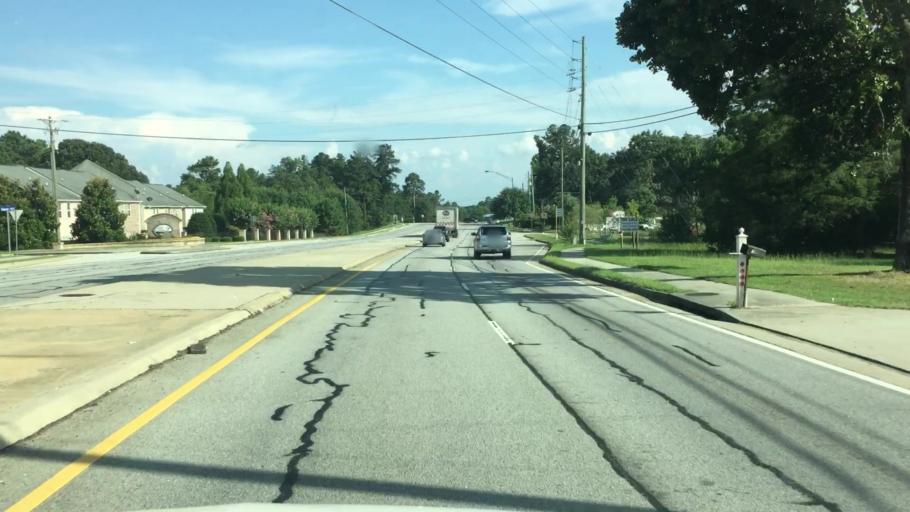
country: US
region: Georgia
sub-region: Gwinnett County
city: Snellville
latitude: 33.8332
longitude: -84.0320
